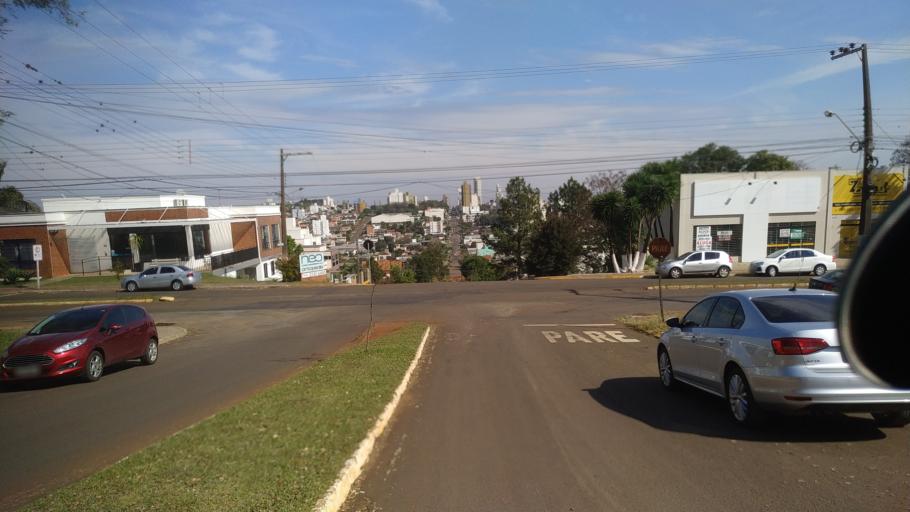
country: BR
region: Santa Catarina
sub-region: Chapeco
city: Chapeco
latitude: -27.1073
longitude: -52.5992
